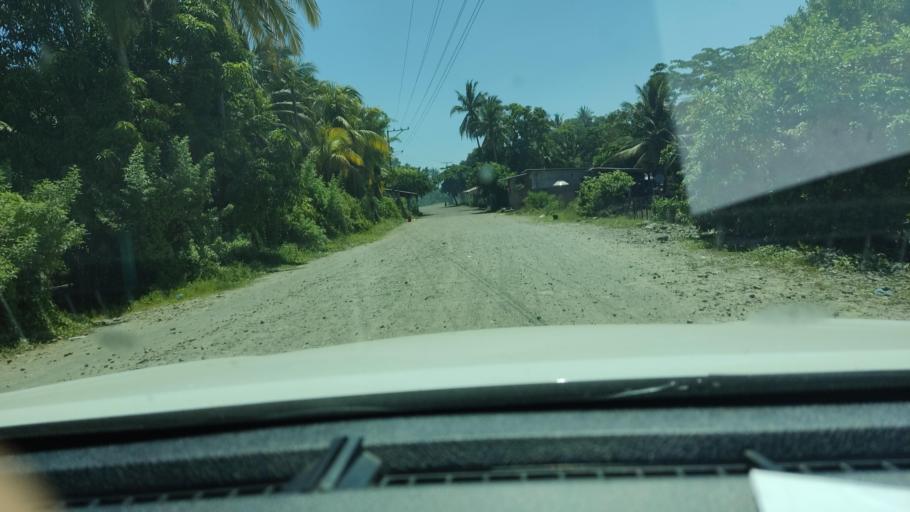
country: SV
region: Ahuachapan
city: San Francisco Menendez
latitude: 13.7646
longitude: -90.1572
